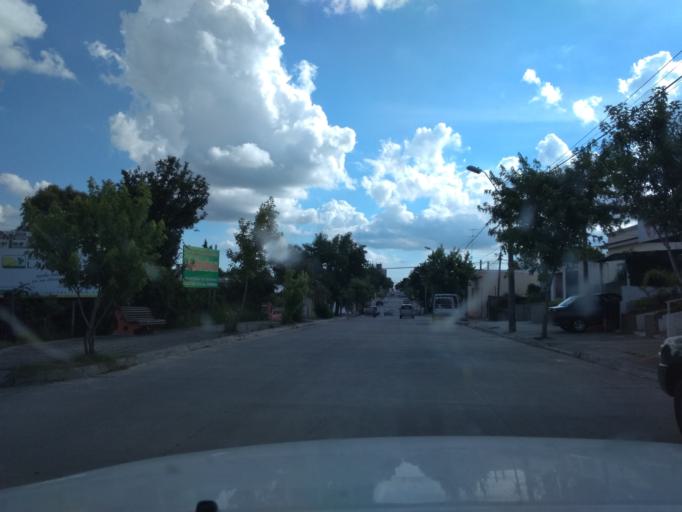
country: UY
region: Florida
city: Florida
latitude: -34.0903
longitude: -56.2152
